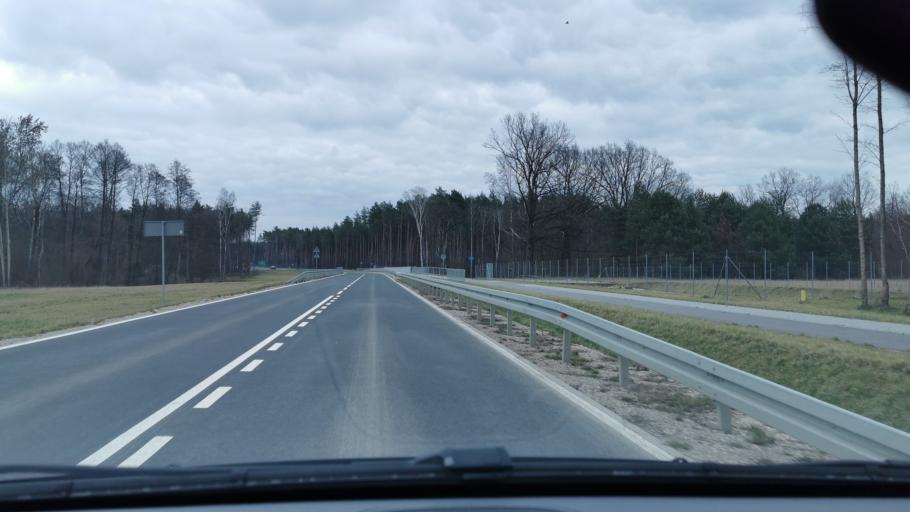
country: PL
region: Masovian Voivodeship
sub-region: Powiat zyrardowski
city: Zyrardow
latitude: 52.0109
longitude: 20.4715
